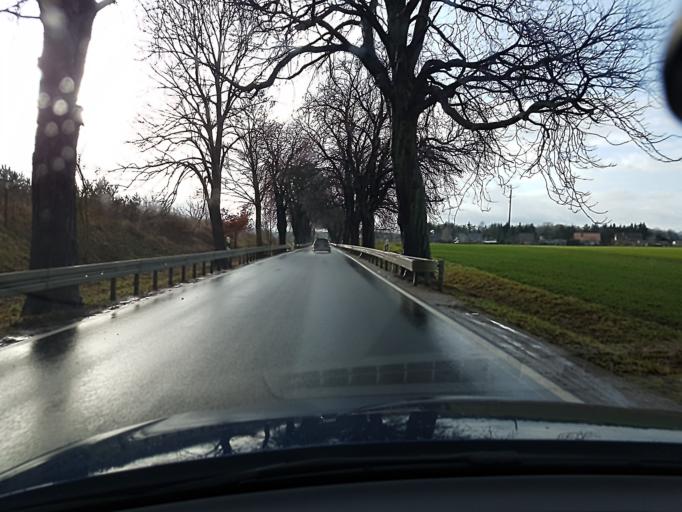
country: DE
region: Mecklenburg-Vorpommern
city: Bad Sulze
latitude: 54.0719
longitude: 12.6791
